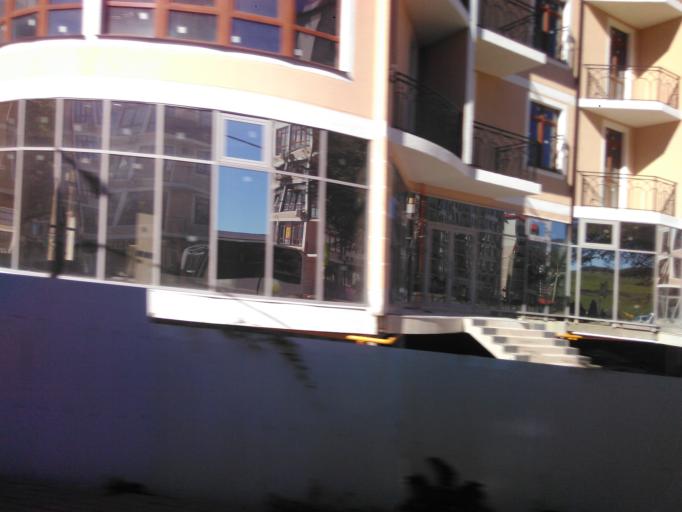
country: RU
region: Krasnodarskiy
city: Gelendzhik
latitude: 44.5487
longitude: 38.0597
